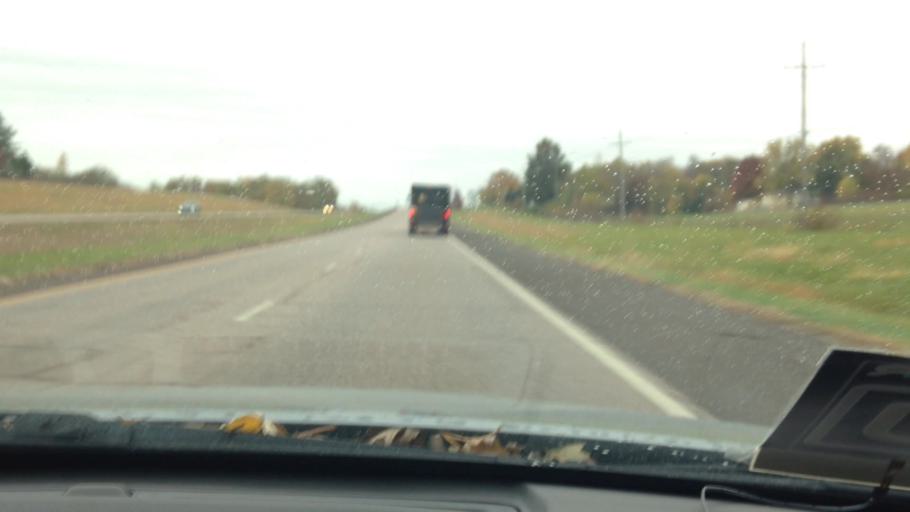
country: US
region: Kansas
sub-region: Leavenworth County
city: Lansing
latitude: 39.2109
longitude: -94.9004
